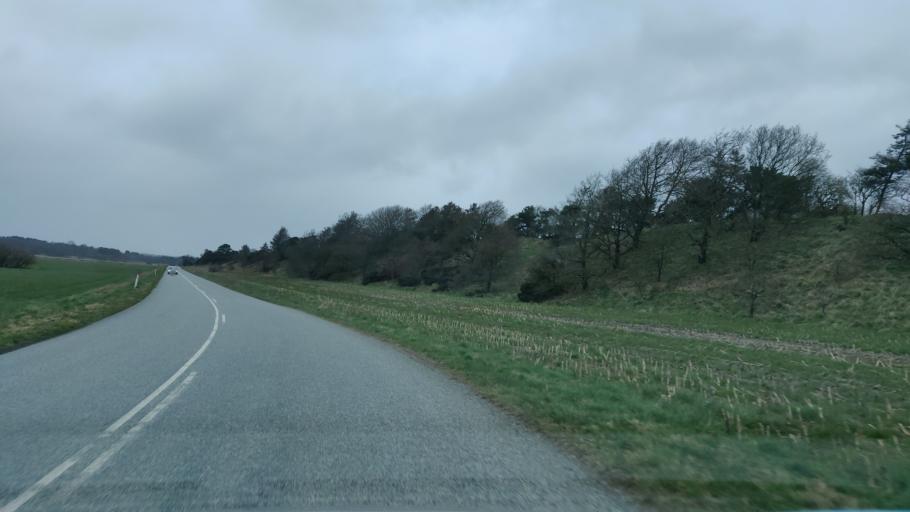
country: DK
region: Central Jutland
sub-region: Skive Kommune
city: Hojslev
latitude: 56.5642
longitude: 9.2499
